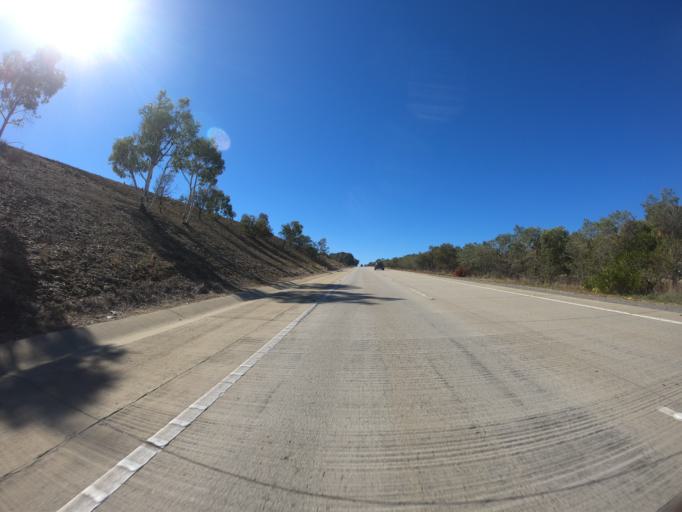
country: AU
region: New South Wales
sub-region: Yass Valley
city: Gundaroo
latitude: -35.1157
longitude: 149.3552
